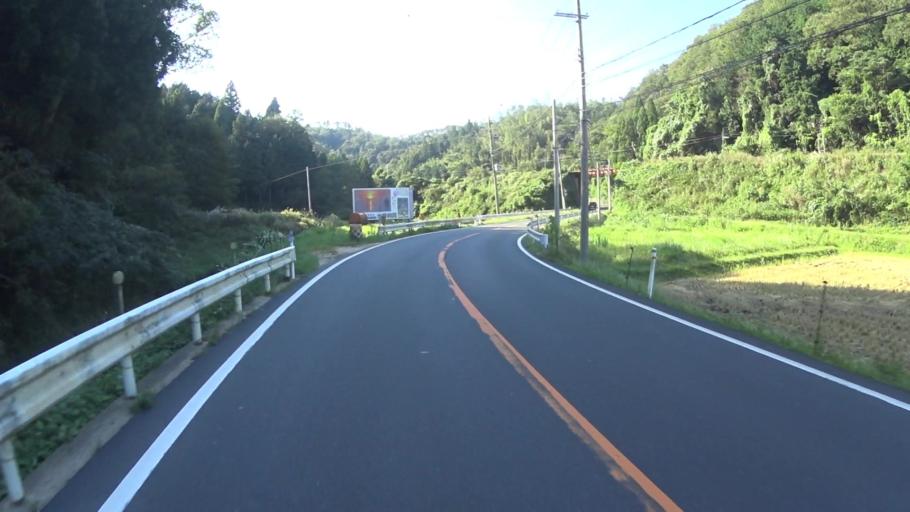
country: JP
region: Kyoto
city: Miyazu
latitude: 35.6608
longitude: 135.0179
